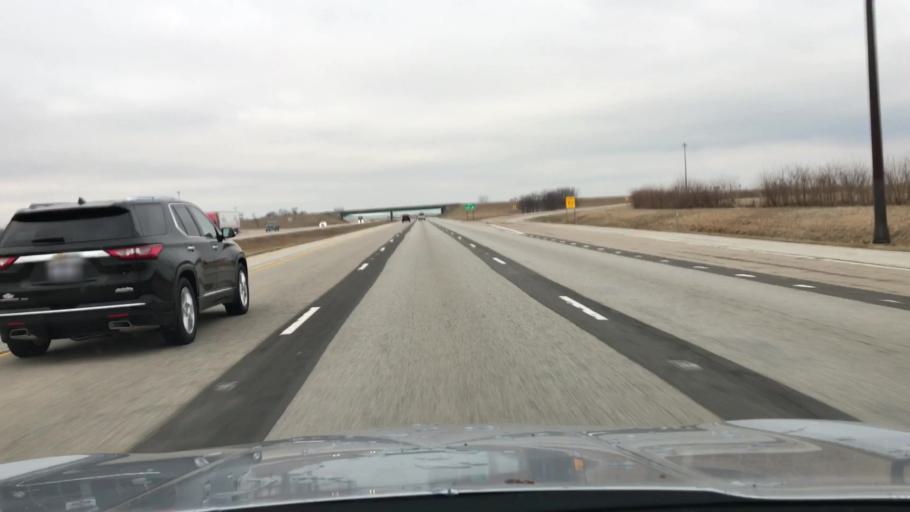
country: US
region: Illinois
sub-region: Logan County
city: Lincoln
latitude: 40.0775
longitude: -89.4376
